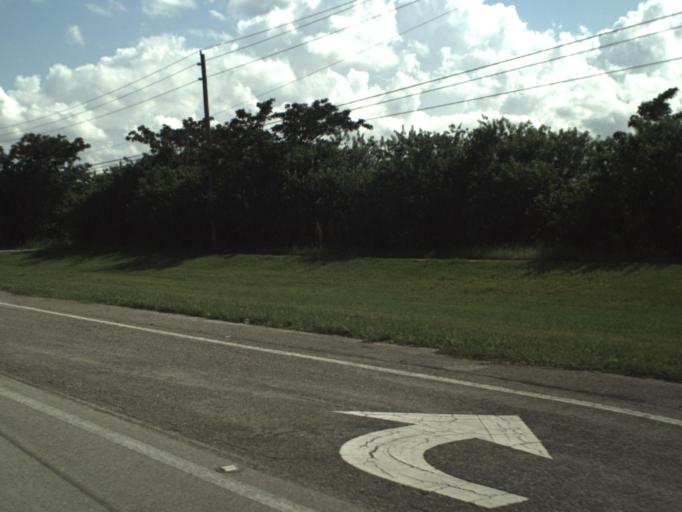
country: US
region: Florida
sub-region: Palm Beach County
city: Villages of Oriole
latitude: 26.4235
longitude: -80.2043
